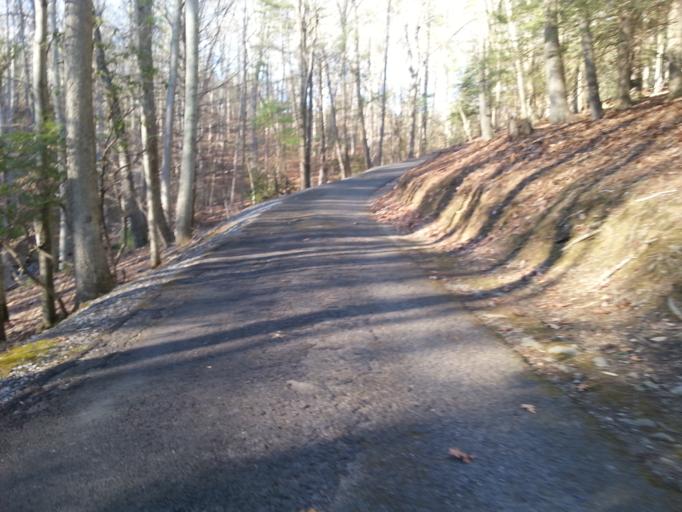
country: US
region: West Virginia
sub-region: Mercer County
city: Athens
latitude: 37.5379
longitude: -80.9826
